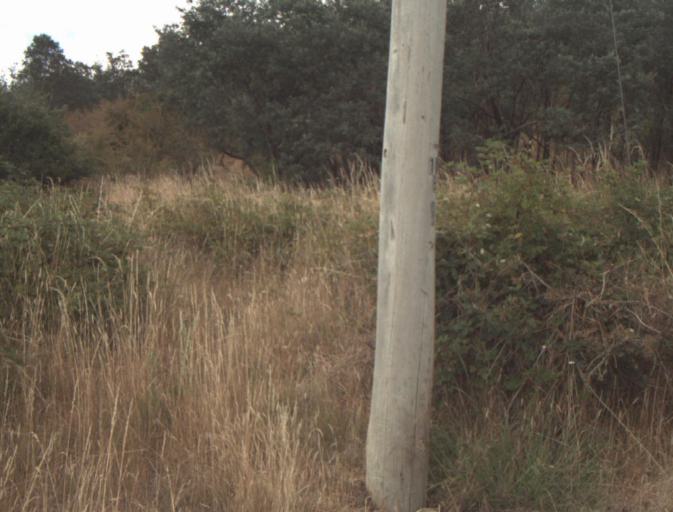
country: AU
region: Tasmania
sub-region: Launceston
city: Summerhill
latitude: -41.4771
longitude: 147.1598
